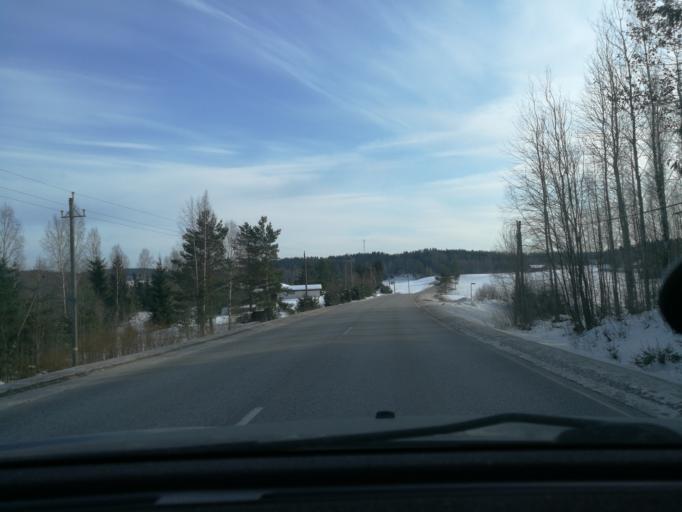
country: FI
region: Uusimaa
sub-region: Helsinki
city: Saukkola
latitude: 60.3951
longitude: 24.0728
